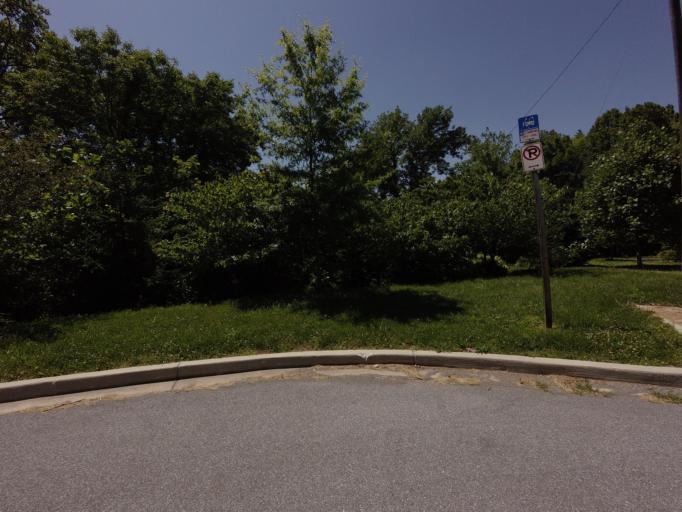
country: US
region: Maryland
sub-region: Frederick County
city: Brunswick
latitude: 39.3329
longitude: -77.6832
